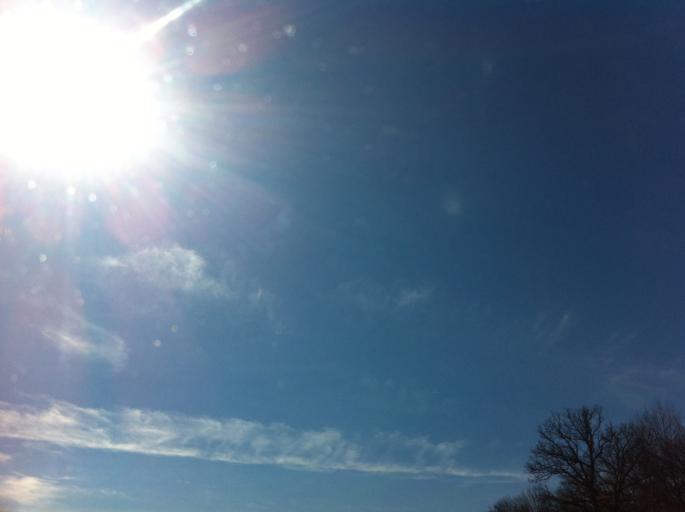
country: US
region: Wisconsin
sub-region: Rock County
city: Edgerton
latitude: 42.8210
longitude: -89.0238
